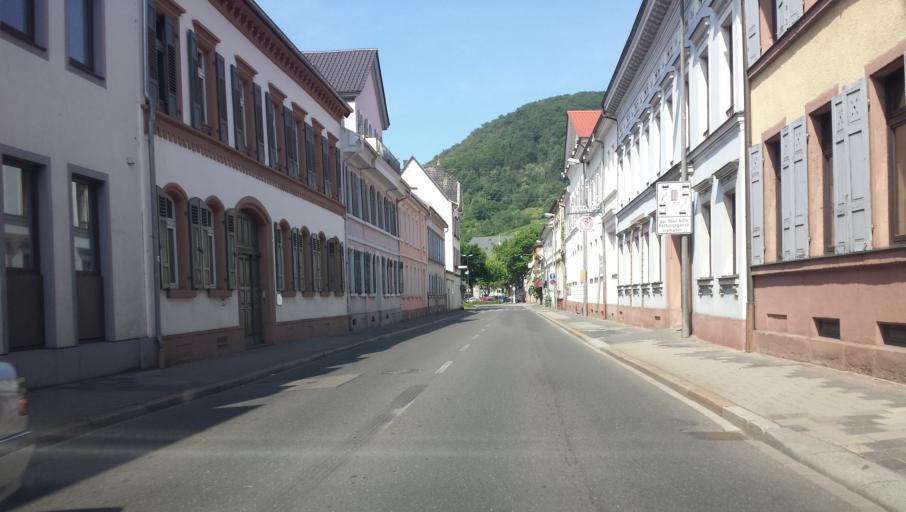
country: DE
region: Rheinland-Pfalz
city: Neustadt
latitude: 49.3556
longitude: 8.1401
